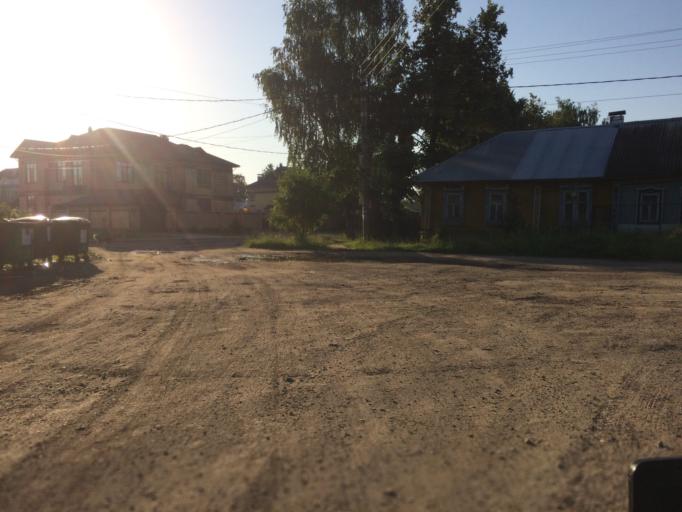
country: RU
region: Mariy-El
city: Yoshkar-Ola
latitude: 56.6507
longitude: 47.9059
